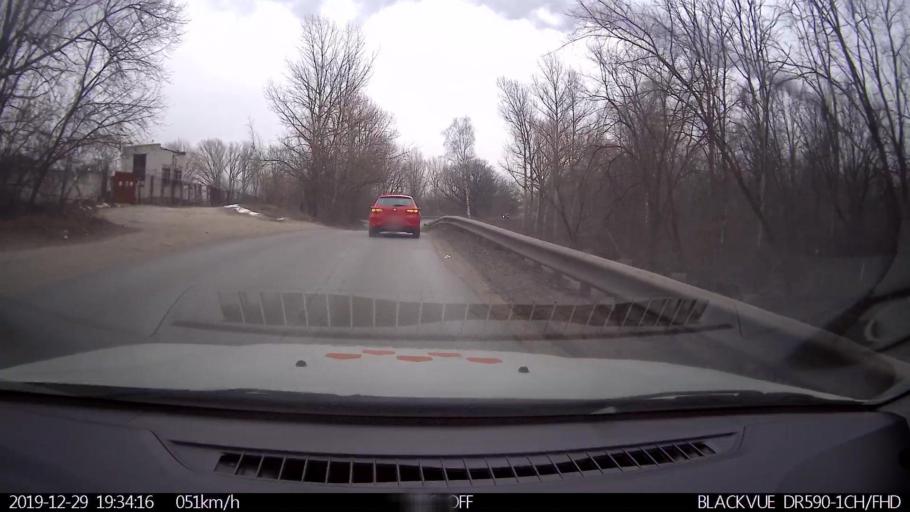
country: RU
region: Nizjnij Novgorod
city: Neklyudovo
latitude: 56.3582
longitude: 43.8892
